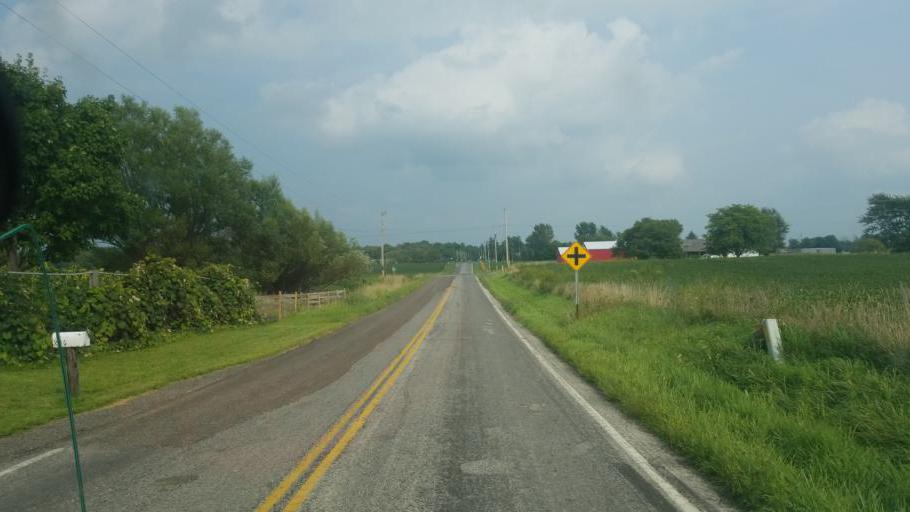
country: US
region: Ohio
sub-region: Wayne County
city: West Salem
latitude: 41.0582
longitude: -82.1829
